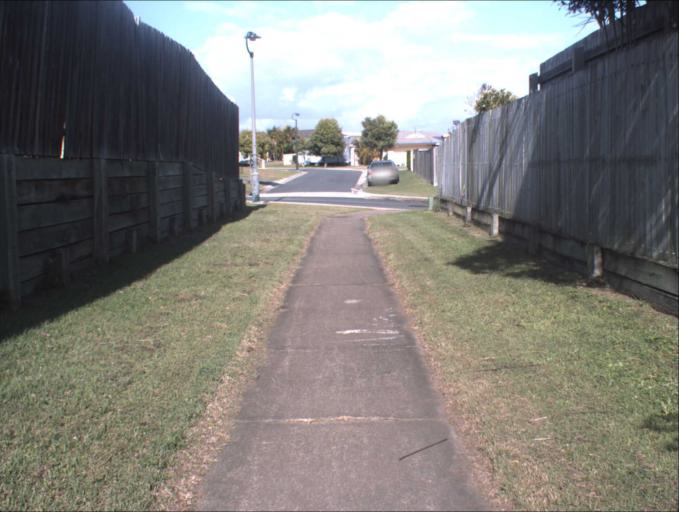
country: AU
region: Queensland
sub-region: Logan
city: Park Ridge South
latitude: -27.6799
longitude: 153.0566
